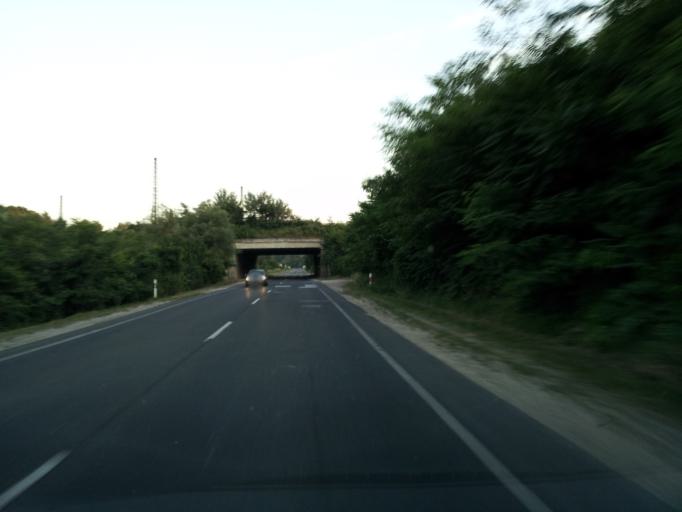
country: HU
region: Fejer
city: Szarliget
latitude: 47.5531
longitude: 18.4468
